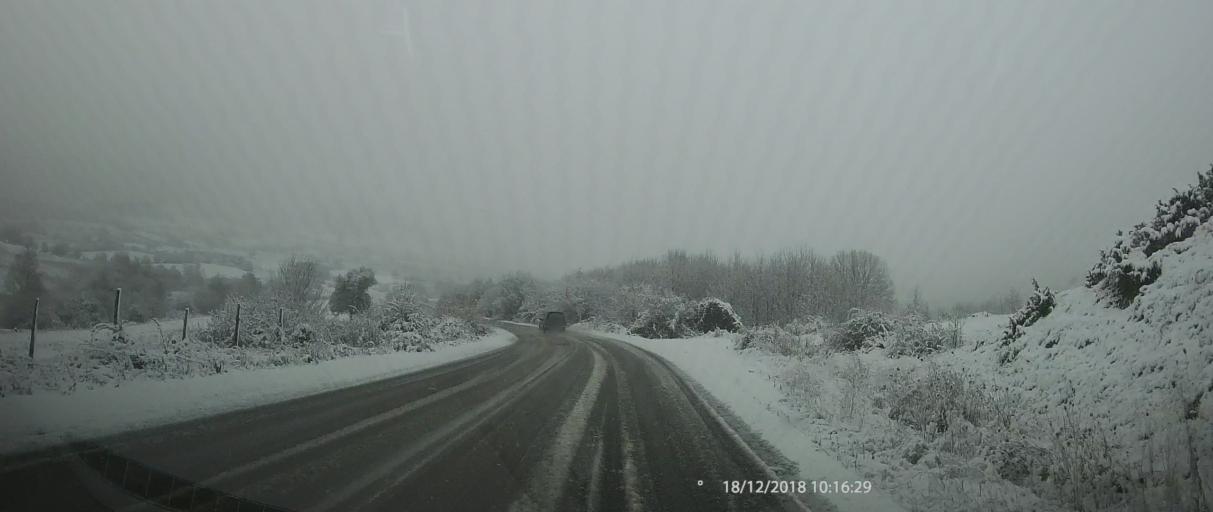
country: GR
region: Thessaly
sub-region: Nomos Larisis
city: Livadi
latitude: 40.1163
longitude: 22.2103
